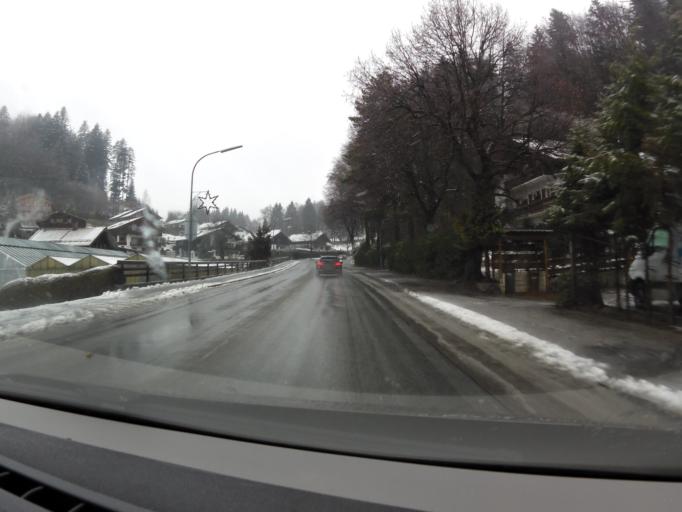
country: DE
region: Bavaria
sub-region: Upper Bavaria
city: Bad Wiessee
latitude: 47.7211
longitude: 11.7172
